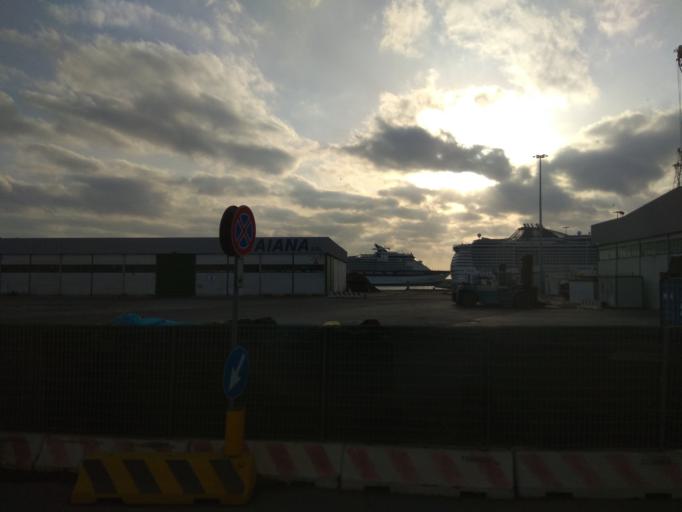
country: IT
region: Latium
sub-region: Citta metropolitana di Roma Capitale
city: Civitavecchia
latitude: 42.1038
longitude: 11.7801
